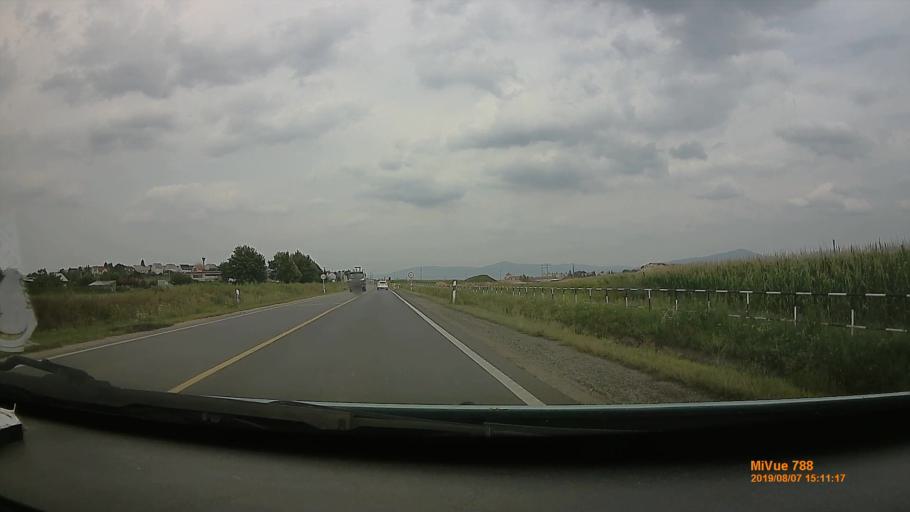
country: HU
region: Borsod-Abauj-Zemplen
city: Encs
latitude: 48.3311
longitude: 21.0990
